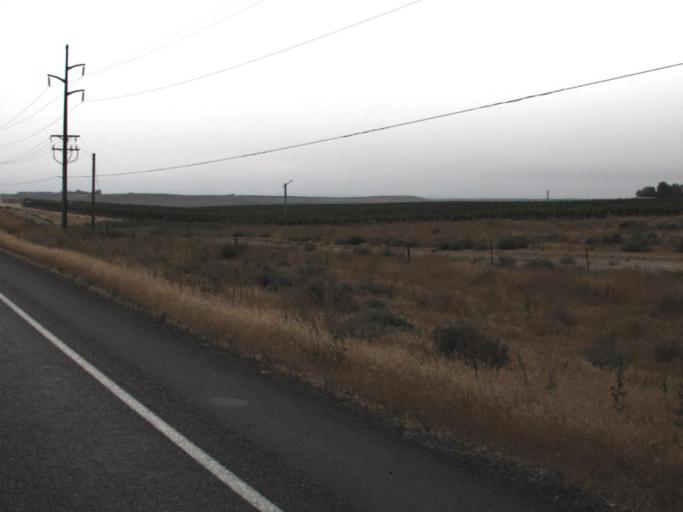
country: US
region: Oregon
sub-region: Morrow County
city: Irrigon
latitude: 45.9972
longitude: -119.6029
